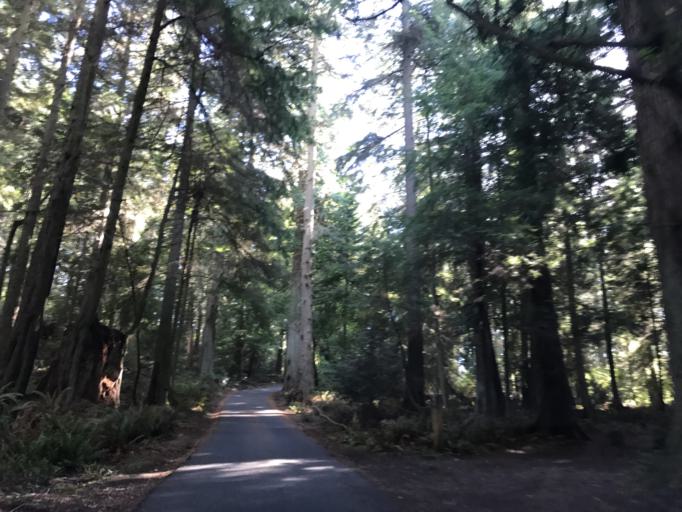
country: US
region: Washington
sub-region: Skagit County
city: Anacortes
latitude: 48.4941
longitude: -122.6929
